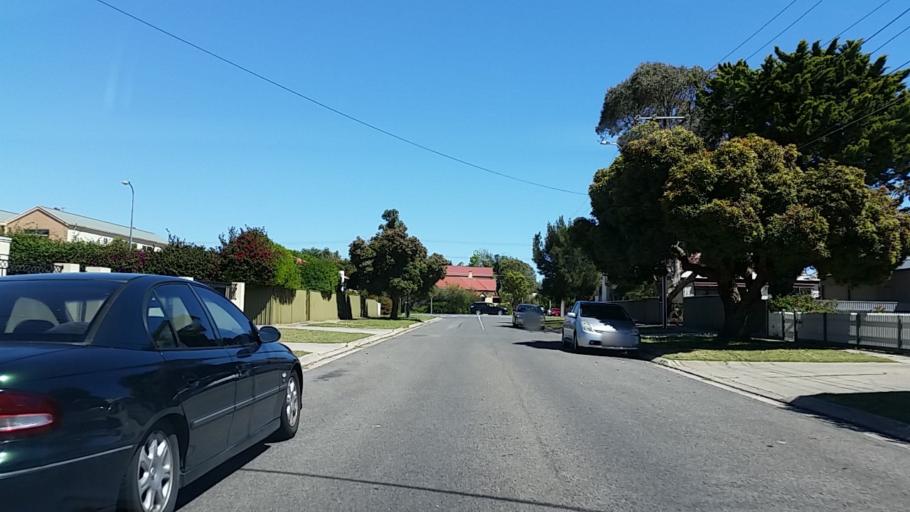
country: AU
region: South Australia
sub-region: Charles Sturt
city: Grange
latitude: -34.9065
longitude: 138.4953
